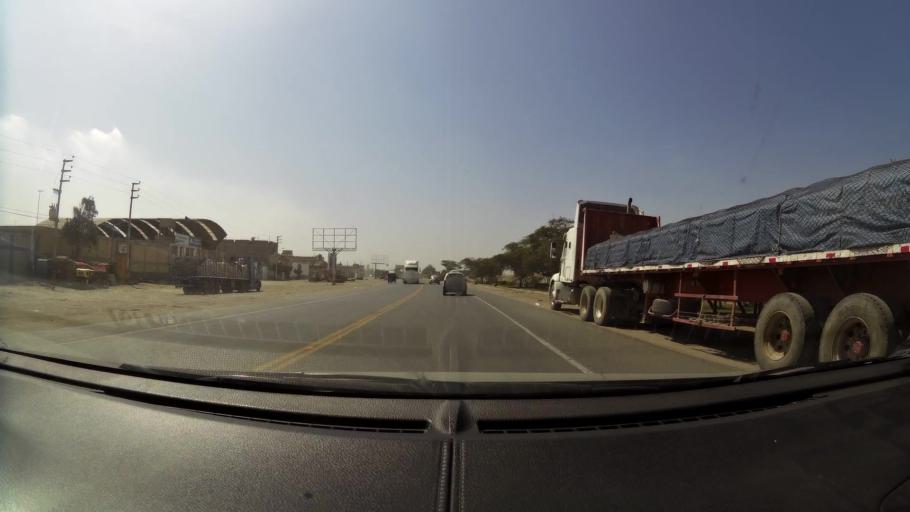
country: PE
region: Lambayeque
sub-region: Provincia de Chiclayo
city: Chiclayo
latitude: -6.8041
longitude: -79.8294
